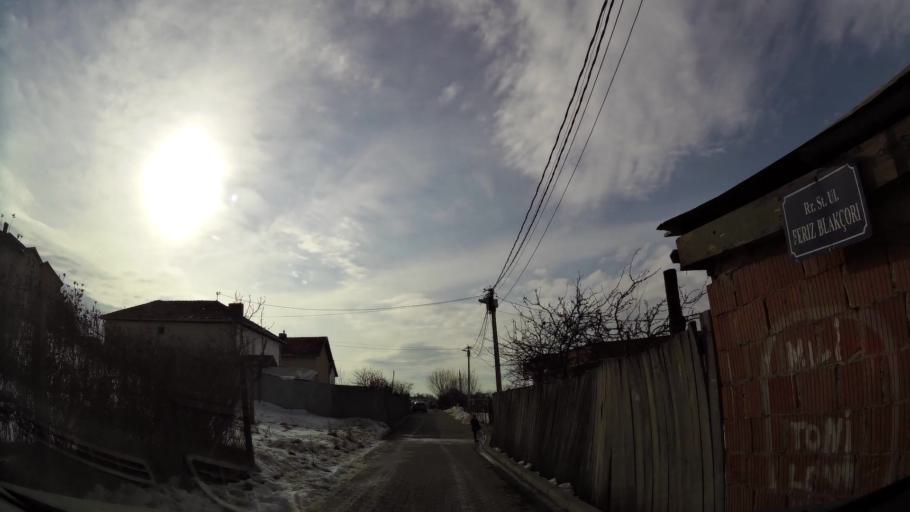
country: XK
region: Pristina
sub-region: Komuna e Prishtines
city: Pristina
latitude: 42.6762
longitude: 21.1529
